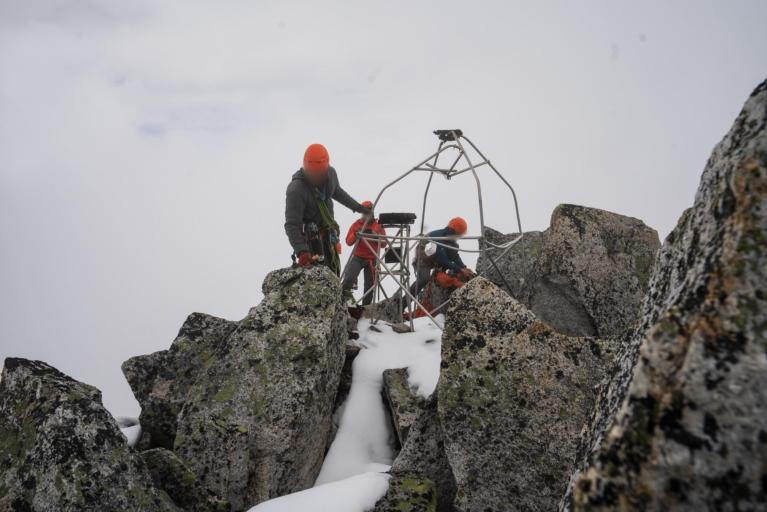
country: RU
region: Transbaikal Territory
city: Chara
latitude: 56.8643
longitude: 117.5769
